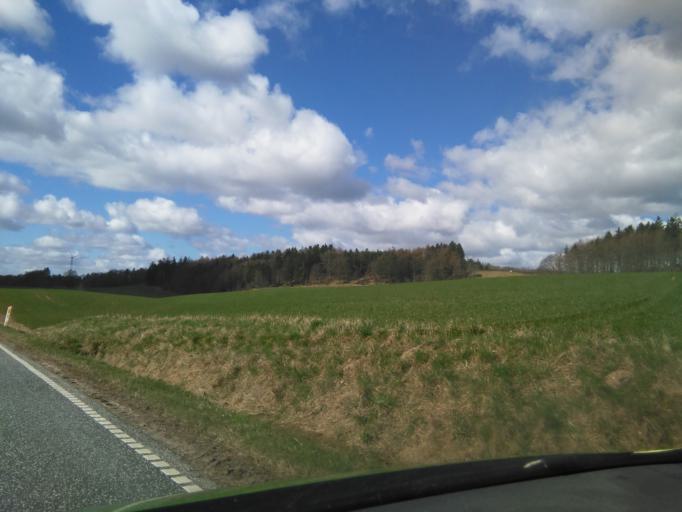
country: DK
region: Central Jutland
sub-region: Horsens Kommune
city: Braedstrup
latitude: 56.0260
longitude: 9.5558
